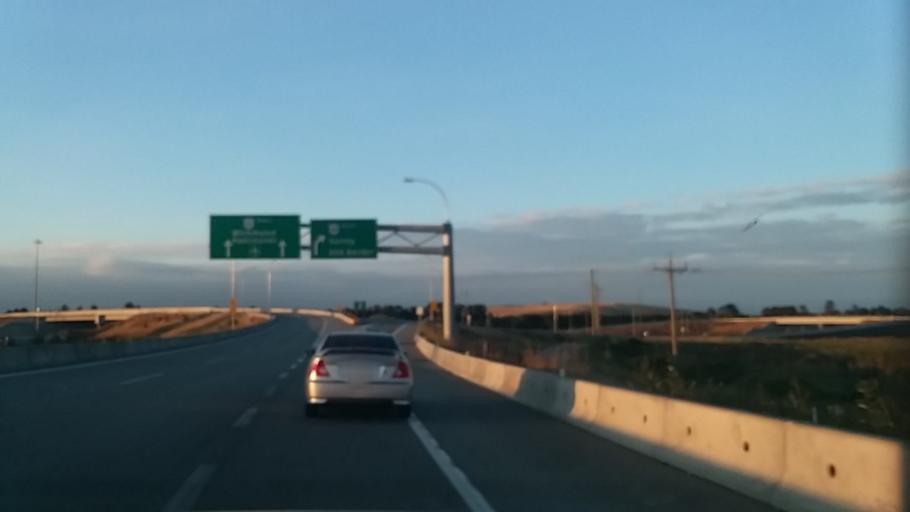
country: CA
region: British Columbia
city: Ladner
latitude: 49.0923
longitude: -123.0241
